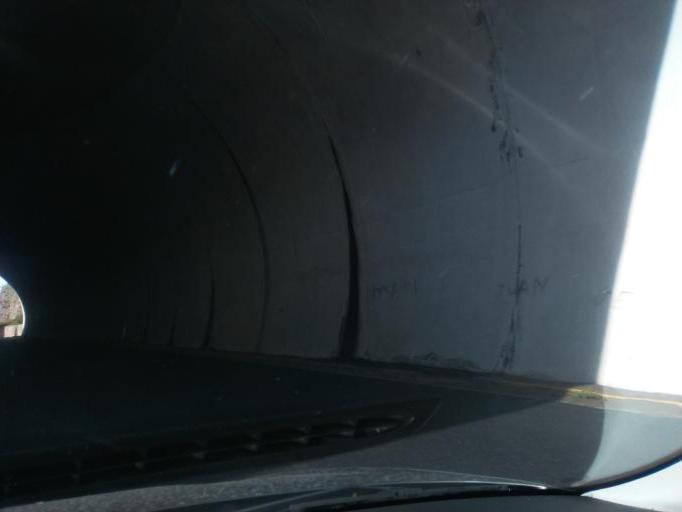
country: MX
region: Guerrero
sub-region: Huitzuco de los Figueroa
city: Ciudad de Huitzuco
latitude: 18.2027
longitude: -99.2073
